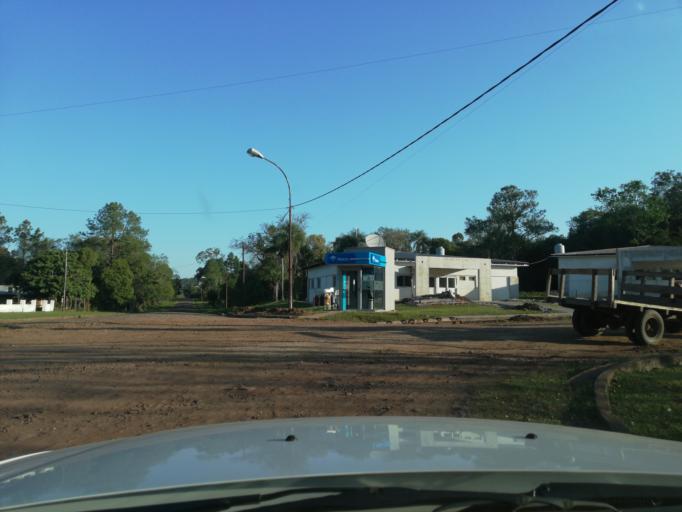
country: AR
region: Misiones
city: Cerro Cora
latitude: -27.6301
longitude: -55.7038
